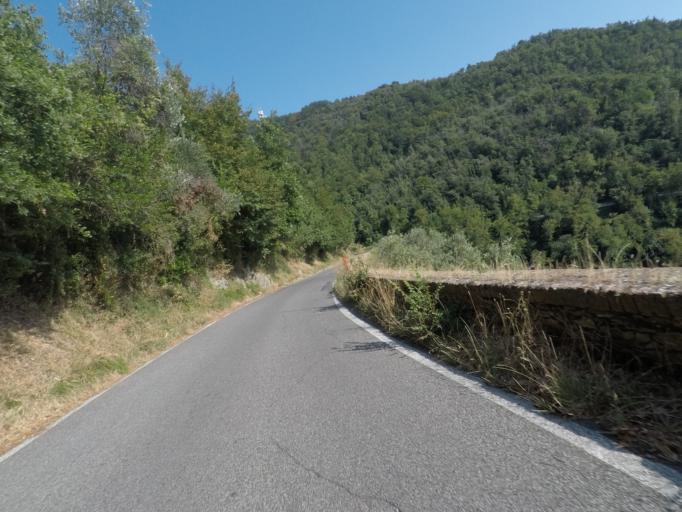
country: IT
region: Liguria
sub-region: Provincia di La Spezia
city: Casano-Dogana-Isola
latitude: 44.0866
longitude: 10.0534
